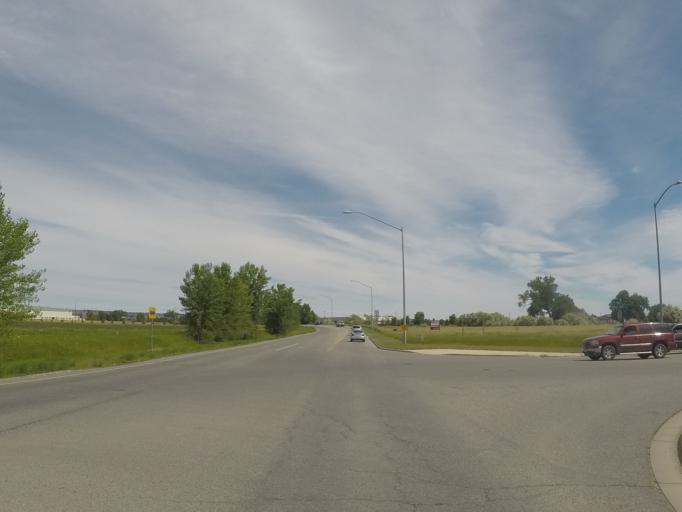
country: US
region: Montana
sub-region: Yellowstone County
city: Billings
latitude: 45.7373
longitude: -108.6085
